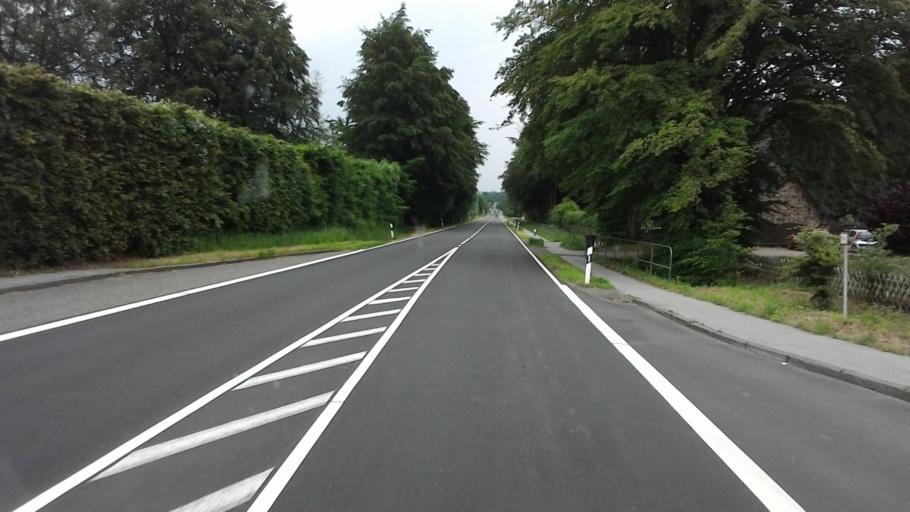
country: DE
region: North Rhine-Westphalia
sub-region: Regierungsbezirk Koln
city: Monschau
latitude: 50.5981
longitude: 6.2498
